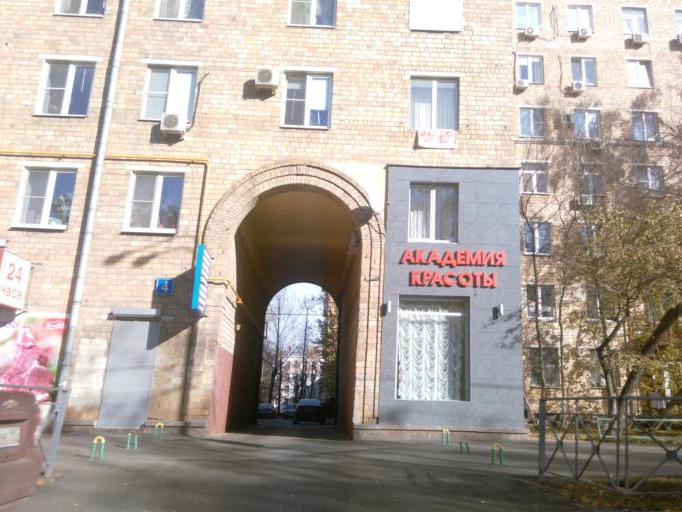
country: RU
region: Moskovskaya
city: Leninskiye Gory
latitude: 55.6967
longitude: 37.5540
